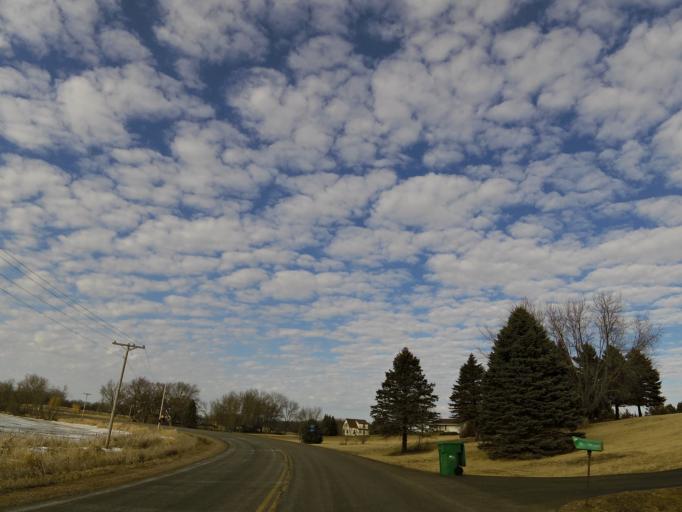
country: US
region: Minnesota
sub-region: Le Sueur County
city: New Prague
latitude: 44.6061
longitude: -93.5538
